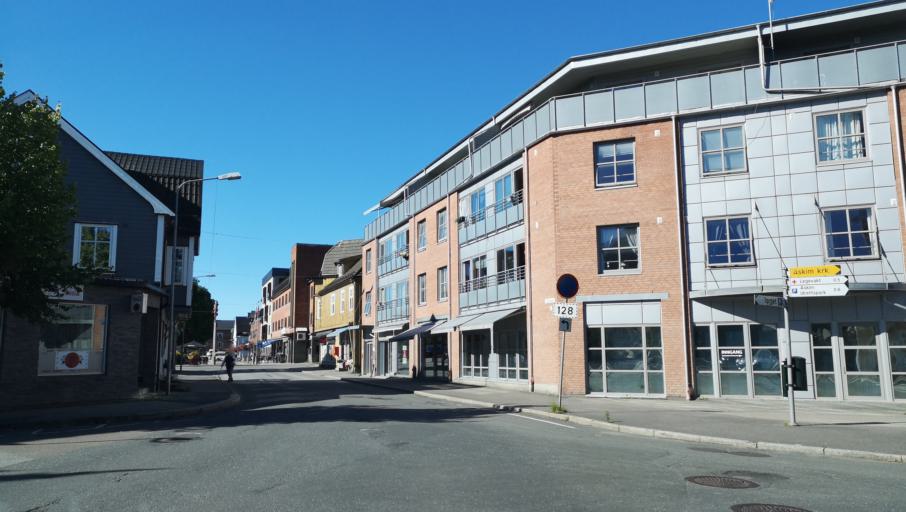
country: NO
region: Ostfold
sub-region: Askim
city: Askim
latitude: 59.5839
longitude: 11.1635
